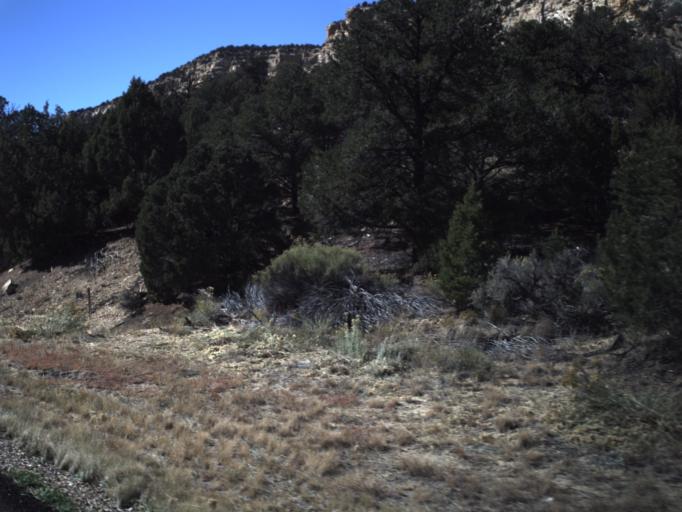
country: US
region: Utah
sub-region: Wayne County
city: Loa
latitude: 37.7317
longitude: -111.7574
